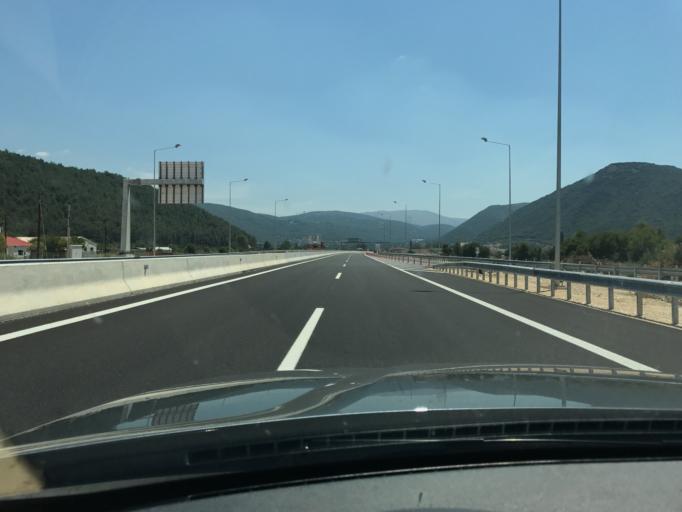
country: GR
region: Epirus
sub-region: Nomos Ioanninon
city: Agia Kyriaki
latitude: 39.5323
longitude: 20.8736
